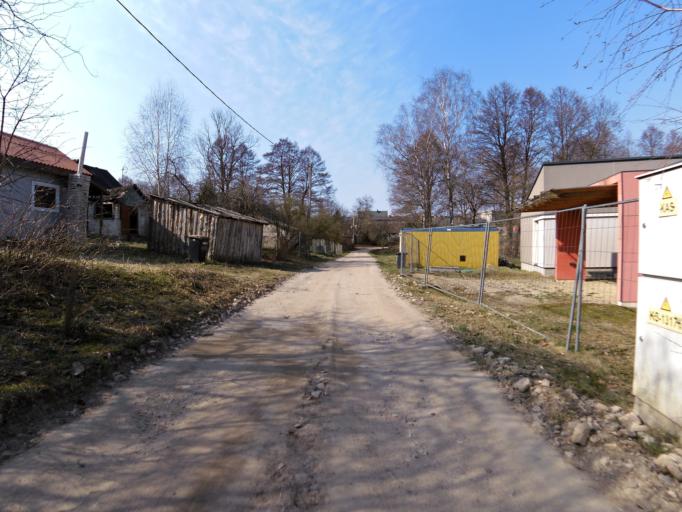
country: LT
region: Vilnius County
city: Pilaite
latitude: 54.6966
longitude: 25.1724
